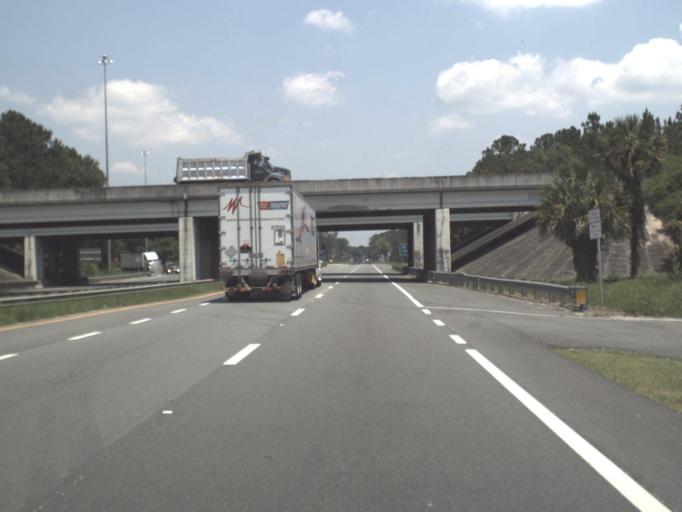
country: US
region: Florida
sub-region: Duval County
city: Baldwin
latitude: 30.2882
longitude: -81.9828
